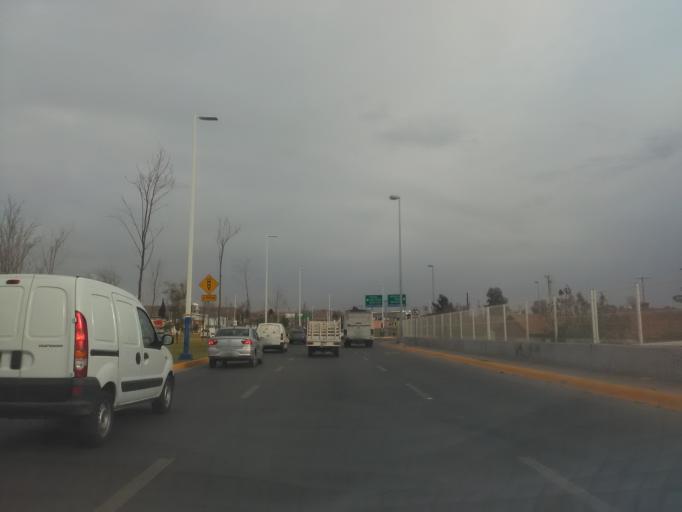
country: MX
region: Durango
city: Victoria de Durango
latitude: 24.0364
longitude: -104.6575
